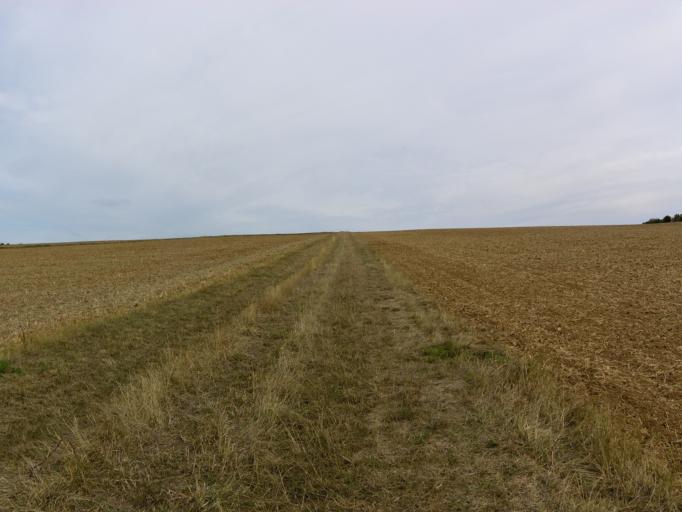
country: DE
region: Bavaria
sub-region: Regierungsbezirk Unterfranken
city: Eisingen
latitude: 49.7754
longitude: 9.8323
